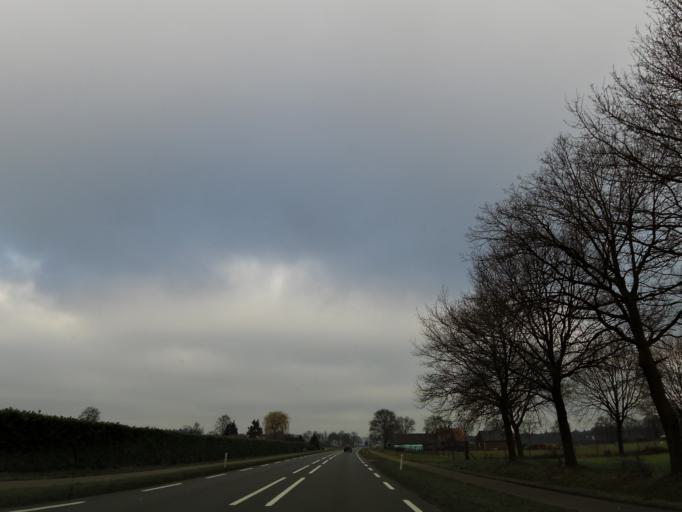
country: NL
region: Limburg
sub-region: Gemeente Venray
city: Venray
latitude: 51.4321
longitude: 5.9502
